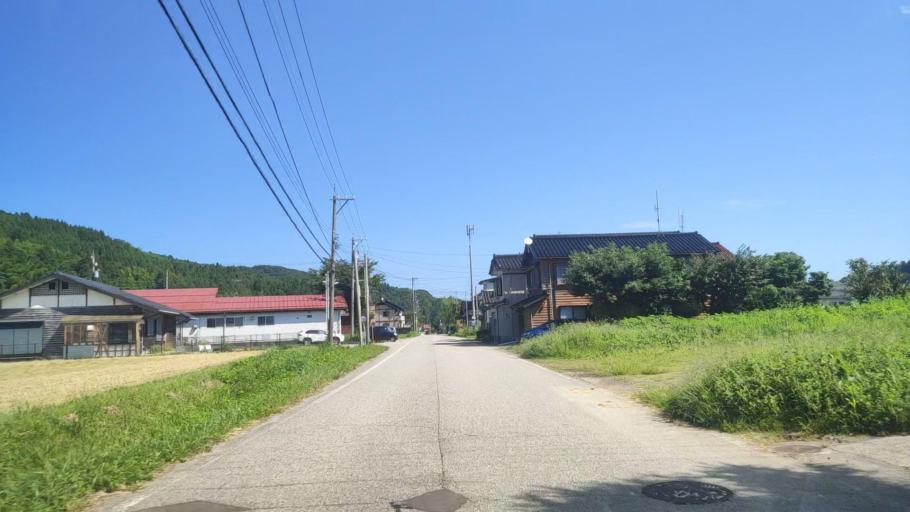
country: JP
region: Ishikawa
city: Nanao
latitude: 37.3773
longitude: 136.8783
